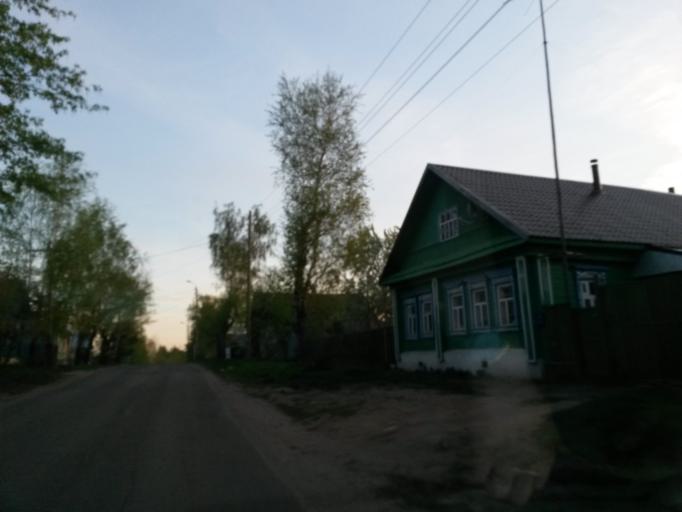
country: RU
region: Jaroslavl
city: Tutayev
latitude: 57.8904
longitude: 39.5570
